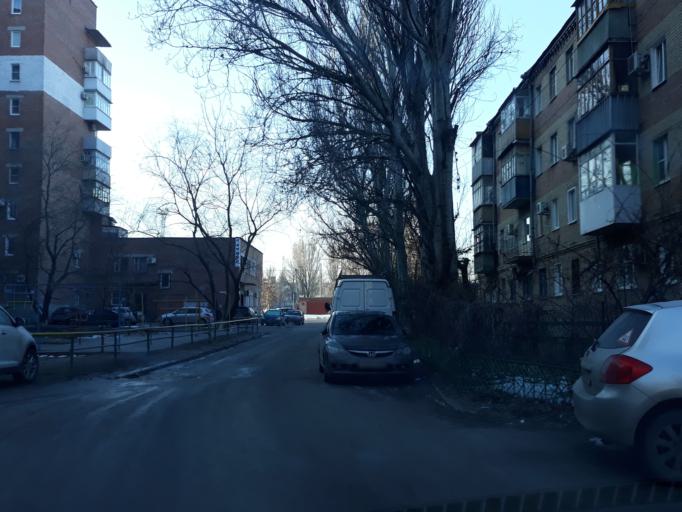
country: RU
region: Rostov
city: Taganrog
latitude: 47.2280
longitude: 38.9076
